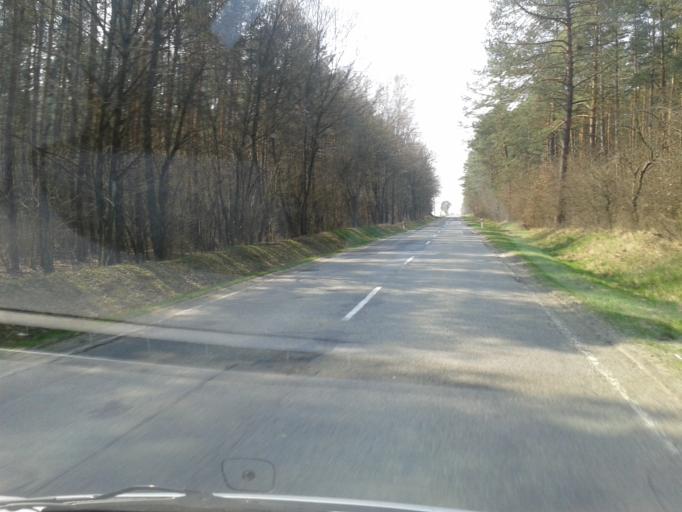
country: PL
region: Subcarpathian Voivodeship
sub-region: Powiat lubaczowski
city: Nowe Siolo
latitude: 50.2927
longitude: 23.1981
